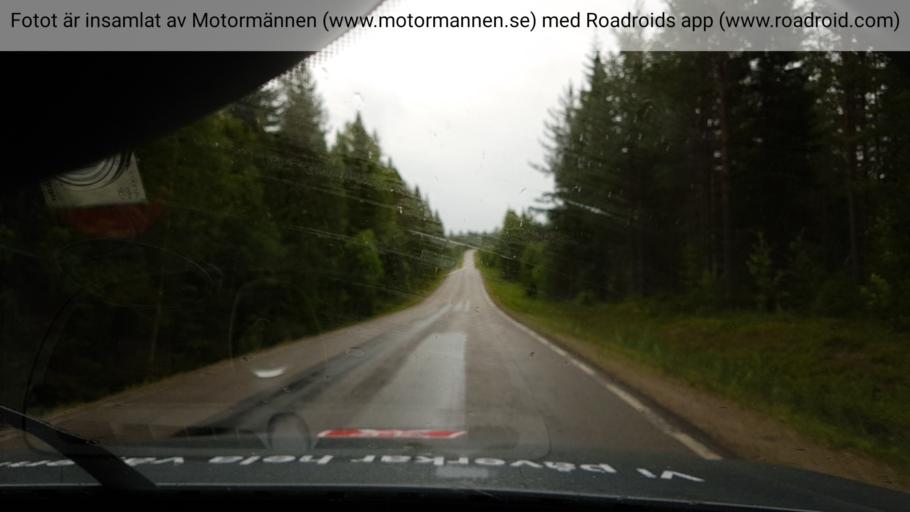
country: SE
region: Jaemtland
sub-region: Braecke Kommun
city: Braecke
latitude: 62.3624
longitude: 15.1797
